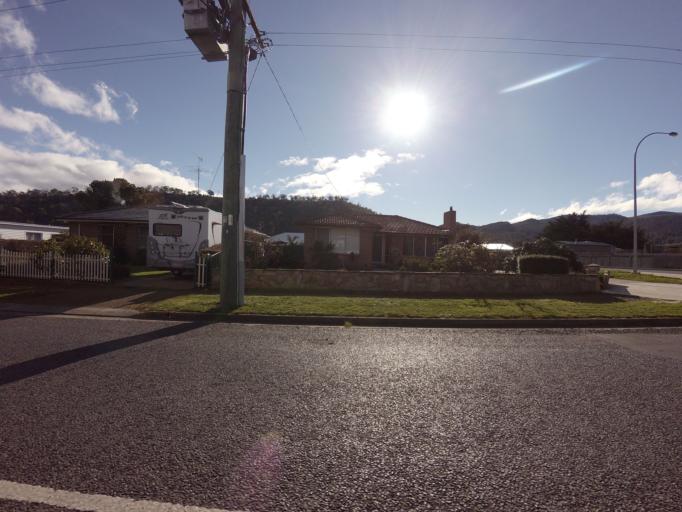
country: AU
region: Tasmania
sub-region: Derwent Valley
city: New Norfolk
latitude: -42.7575
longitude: 147.0488
